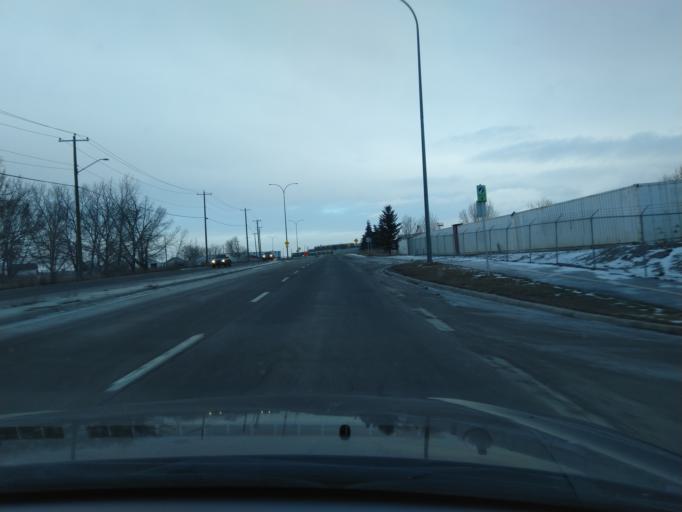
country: CA
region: Alberta
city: Calgary
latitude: 51.1579
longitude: -114.0267
